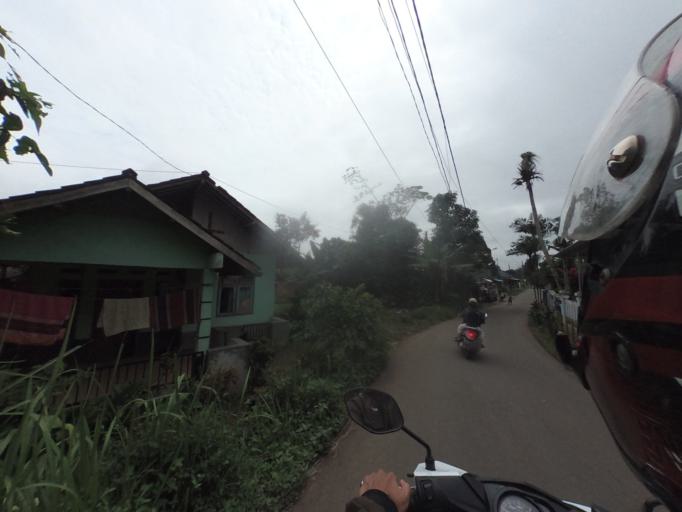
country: ID
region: West Java
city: Bogor
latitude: -6.6384
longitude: 106.7409
